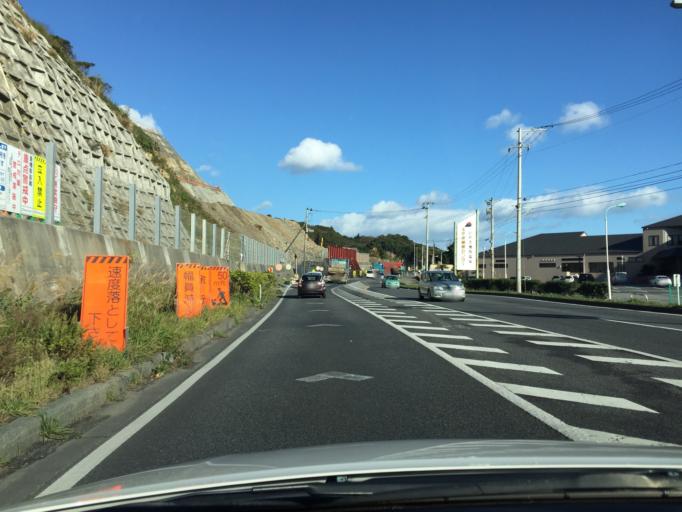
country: JP
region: Fukushima
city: Iwaki
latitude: 37.1114
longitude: 140.9986
